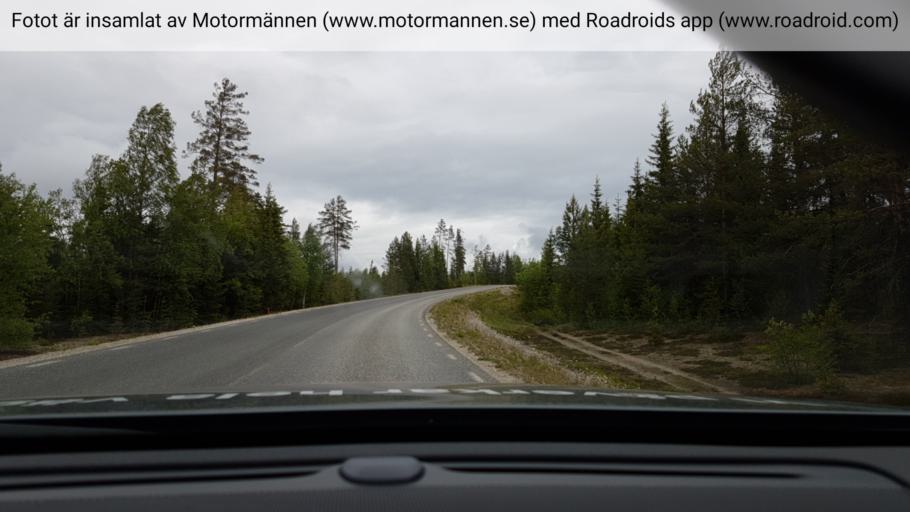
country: SE
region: Vaesterbotten
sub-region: Asele Kommun
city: Insjon
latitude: 64.3533
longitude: 17.8987
